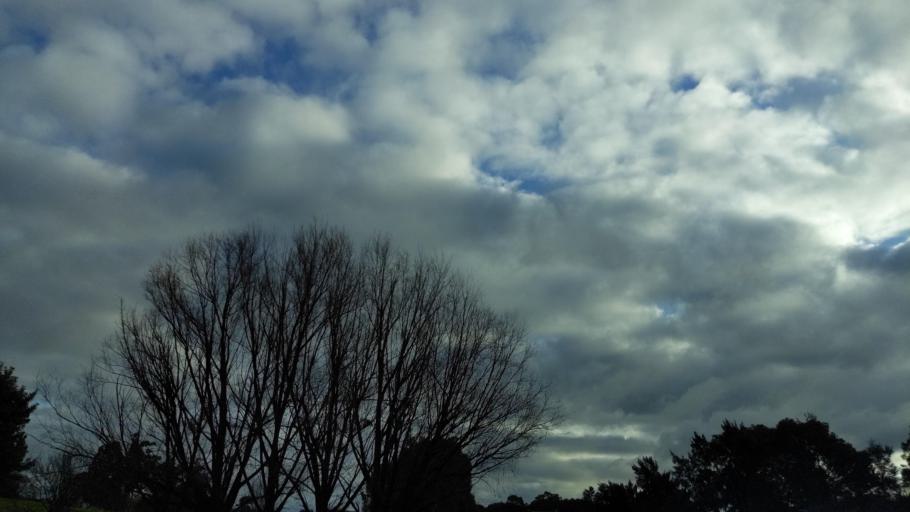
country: AU
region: New South Wales
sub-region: Wagga Wagga
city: Wagga Wagga
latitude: -35.0693
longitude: 147.3851
